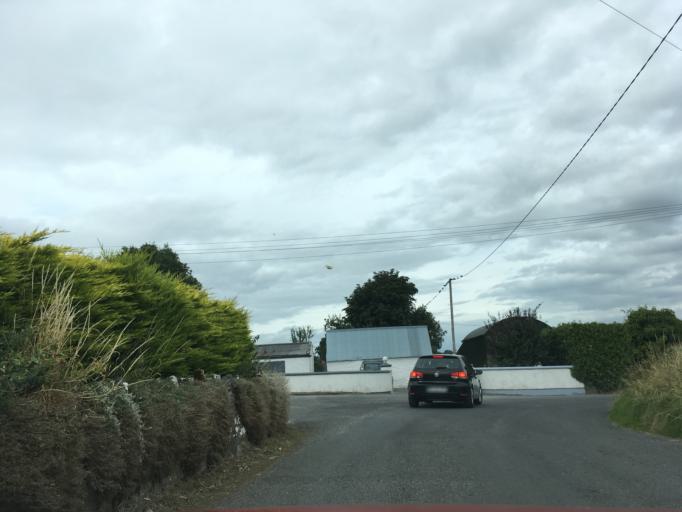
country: IE
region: Munster
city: Cahir
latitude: 52.4718
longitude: -8.0015
